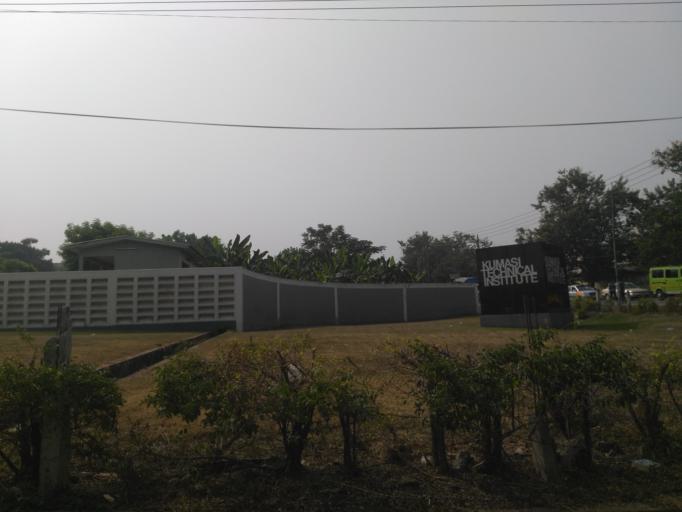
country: GH
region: Ashanti
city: Kumasi
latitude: 6.6942
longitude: -1.6069
